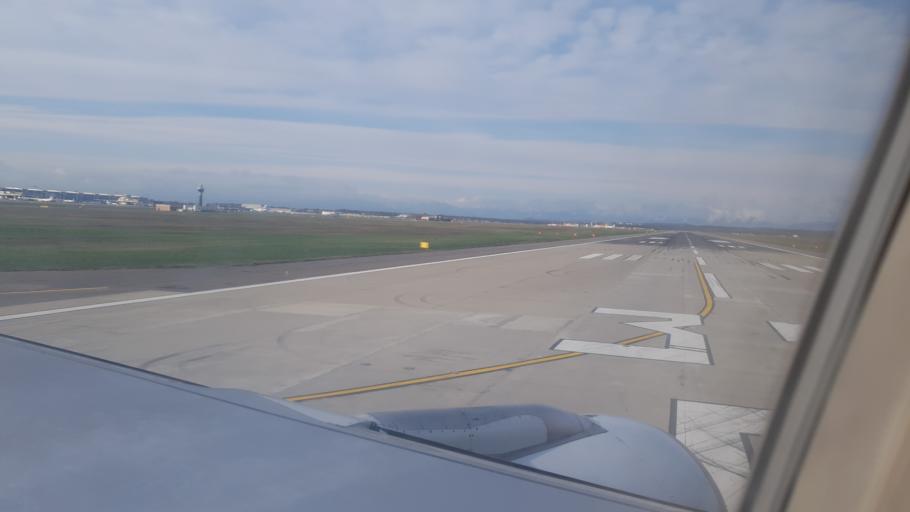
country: IT
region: Lombardy
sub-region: Provincia di Varese
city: Ferno
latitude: 45.6161
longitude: 8.7373
